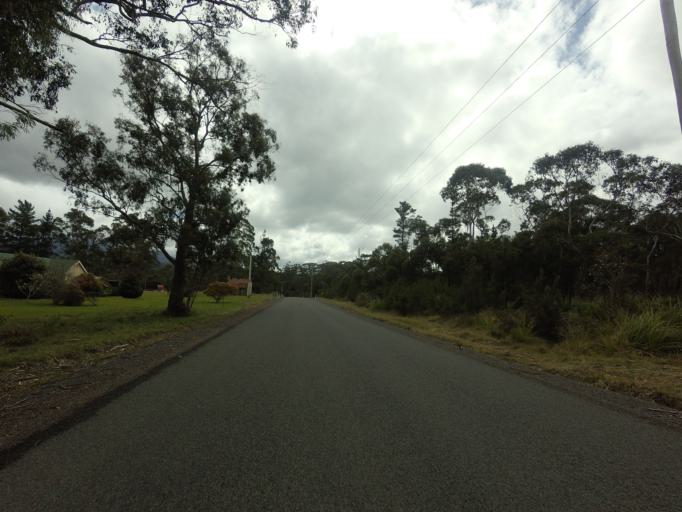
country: AU
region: Tasmania
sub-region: Huon Valley
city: Geeveston
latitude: -43.4354
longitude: 146.9038
